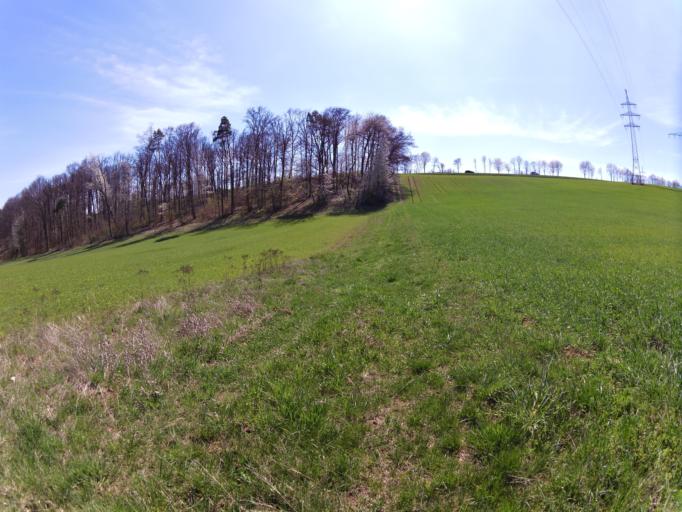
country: DE
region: Bavaria
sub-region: Regierungsbezirk Unterfranken
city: Greussenheim
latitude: 49.8103
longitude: 9.7884
